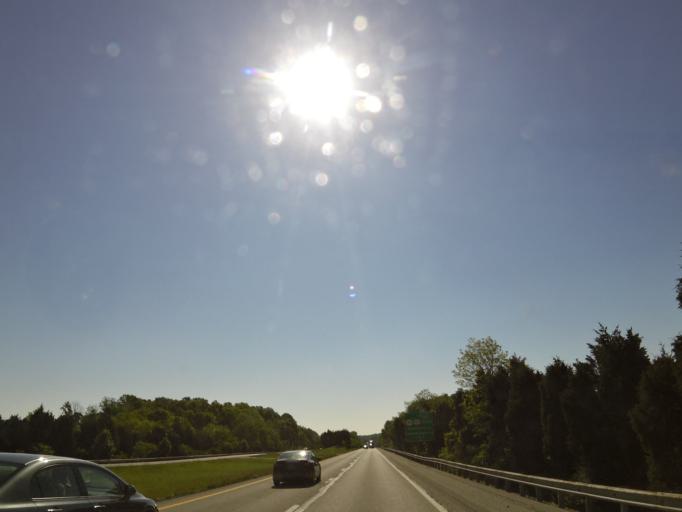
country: US
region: Kentucky
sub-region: Franklin County
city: Frankfort
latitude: 38.1464
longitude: -85.0126
